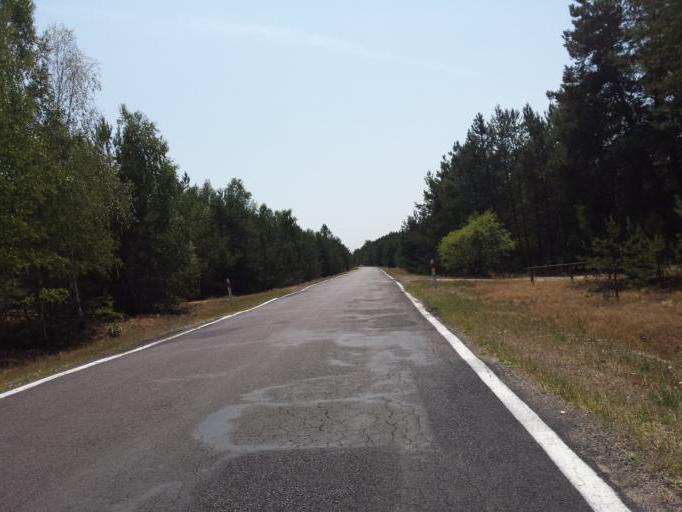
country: PL
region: Lublin Voivodeship
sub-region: Powiat bialski
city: Koden
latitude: 51.8915
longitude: 23.5967
